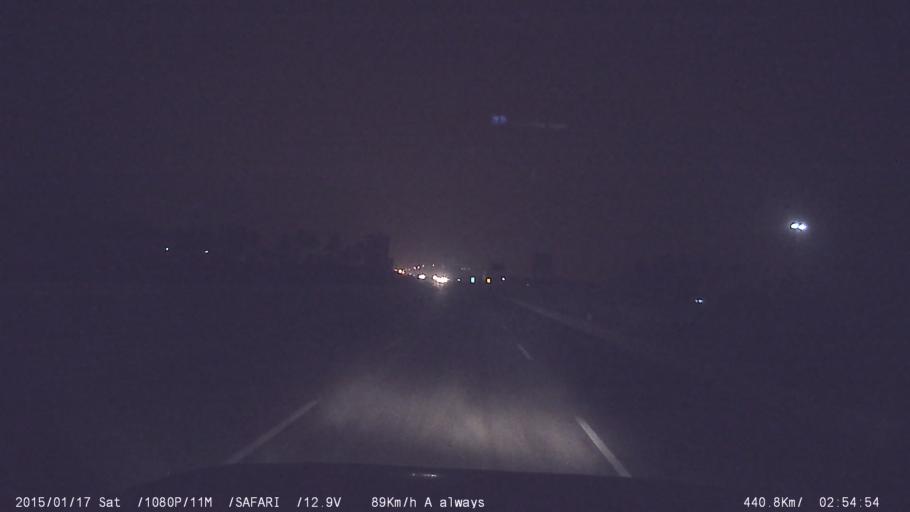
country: IN
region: Tamil Nadu
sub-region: Krishnagiri
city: Hosur
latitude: 12.7809
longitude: 77.7650
